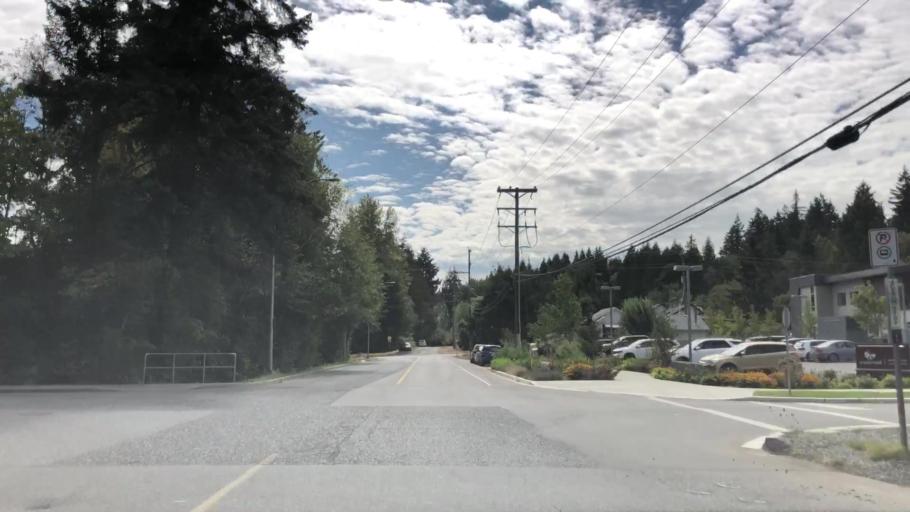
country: CA
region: British Columbia
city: Nanaimo
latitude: 49.1301
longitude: -123.9240
